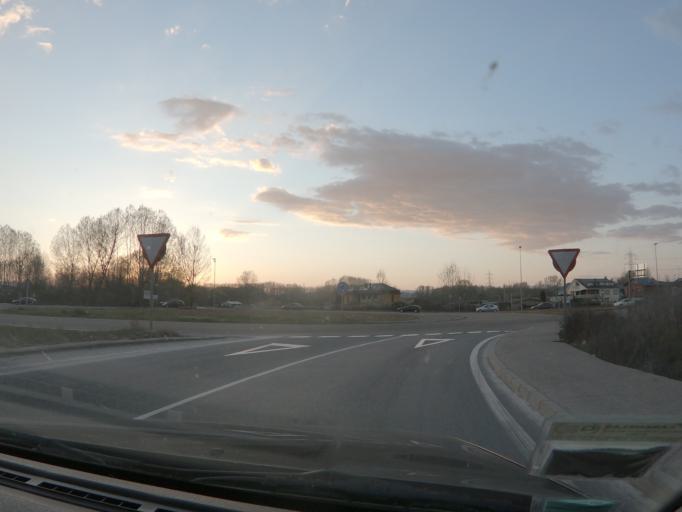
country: ES
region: Castille and Leon
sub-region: Provincia de Leon
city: Ponferrada
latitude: 42.5796
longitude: -6.6078
